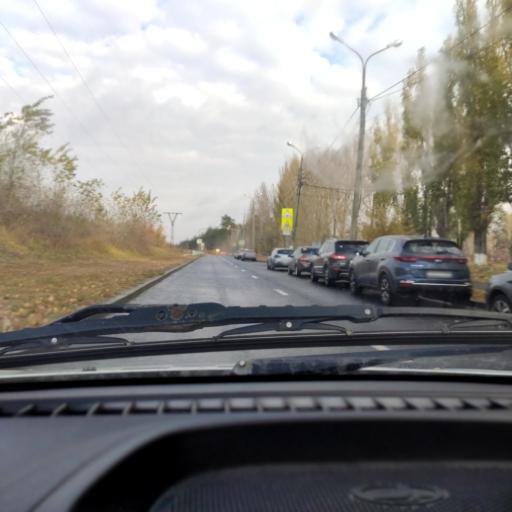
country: RU
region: Samara
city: Zhigulevsk
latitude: 53.4815
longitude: 49.4544
